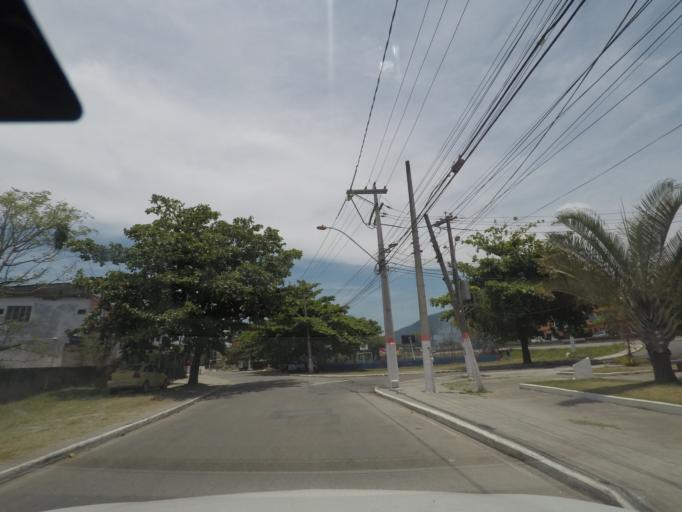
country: BR
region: Rio de Janeiro
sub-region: Marica
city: Marica
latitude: -22.9090
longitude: -42.8355
